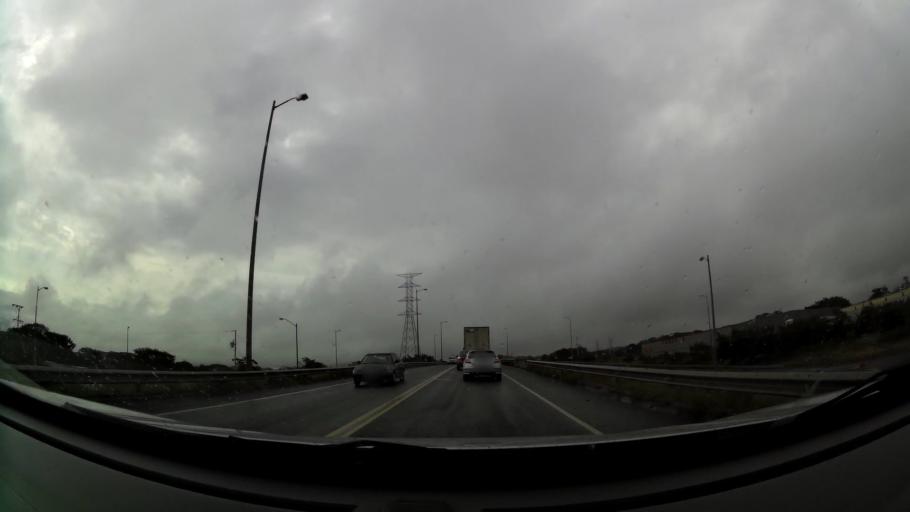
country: CR
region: Alajuela
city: Carrillos
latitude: 9.9837
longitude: -84.2694
